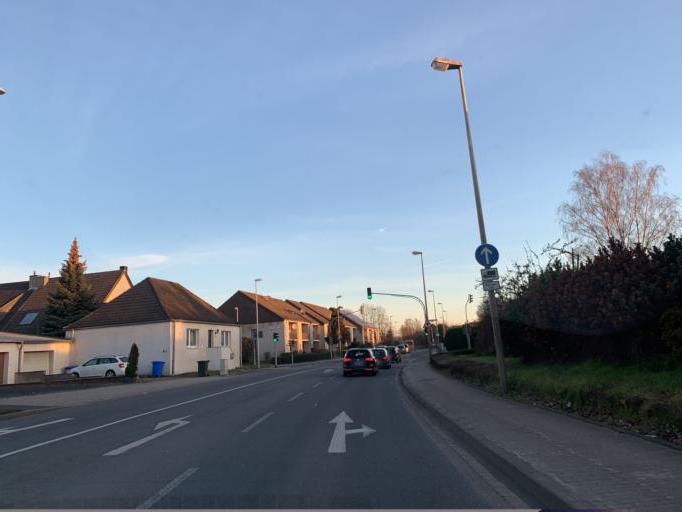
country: DE
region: North Rhine-Westphalia
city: Julich
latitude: 50.9180
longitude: 6.3751
